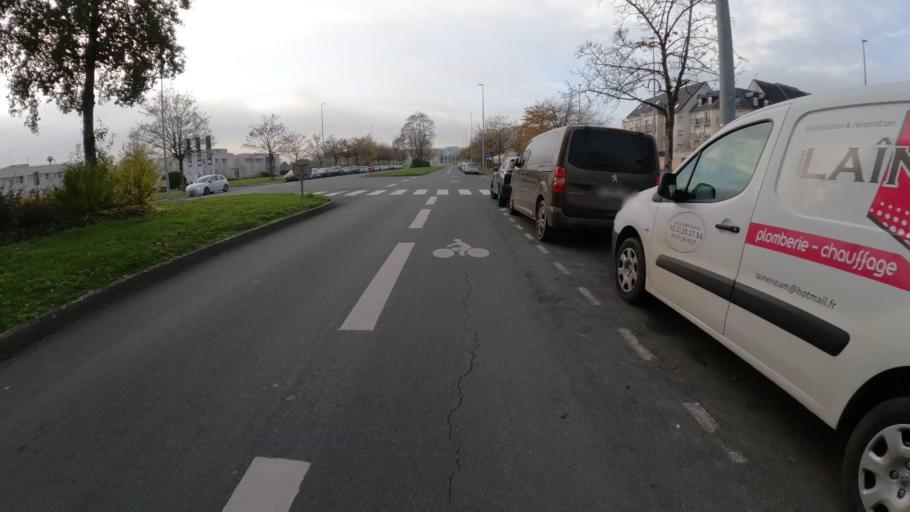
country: FR
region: Lower Normandy
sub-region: Departement du Calvados
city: Epron
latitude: 49.1995
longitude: -0.3807
